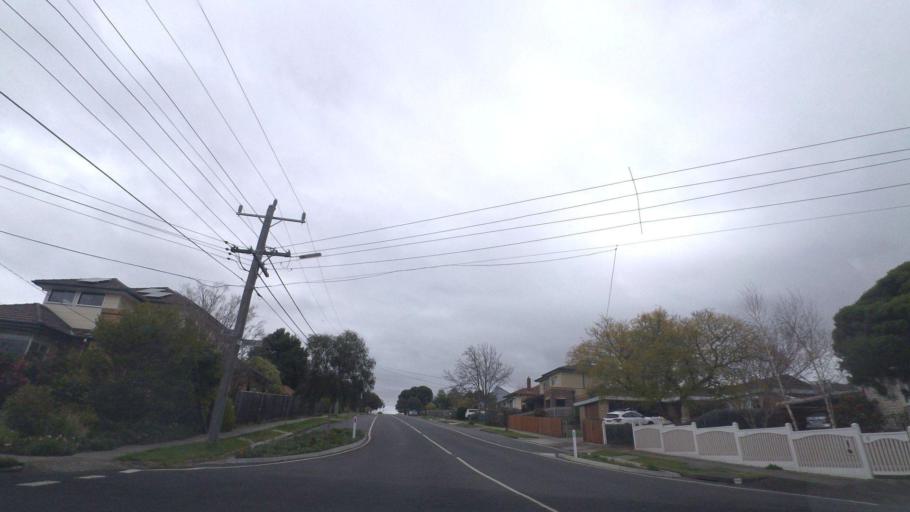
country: AU
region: Victoria
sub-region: Banyule
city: Heidelberg Heights
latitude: -37.7428
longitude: 145.0618
